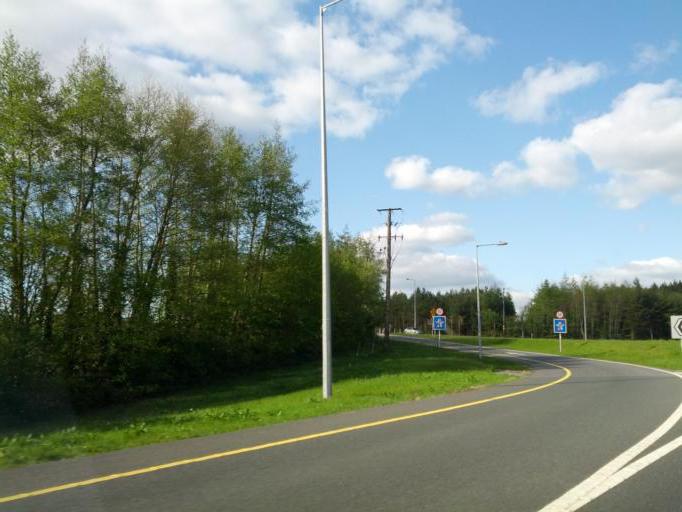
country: IE
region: Leinster
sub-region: An Iarmhi
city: Athlone
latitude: 53.4188
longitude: -7.9836
